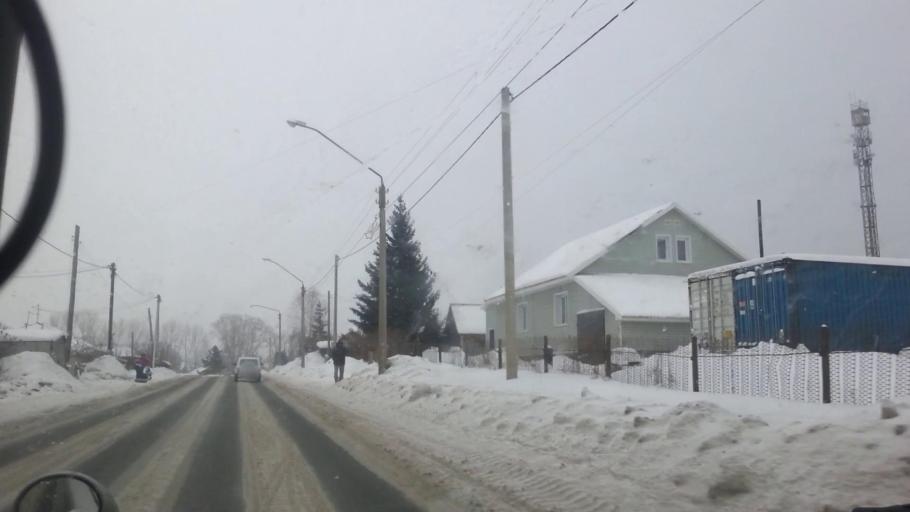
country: RU
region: Altai Krai
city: Vlasikha
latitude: 53.2941
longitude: 83.5748
